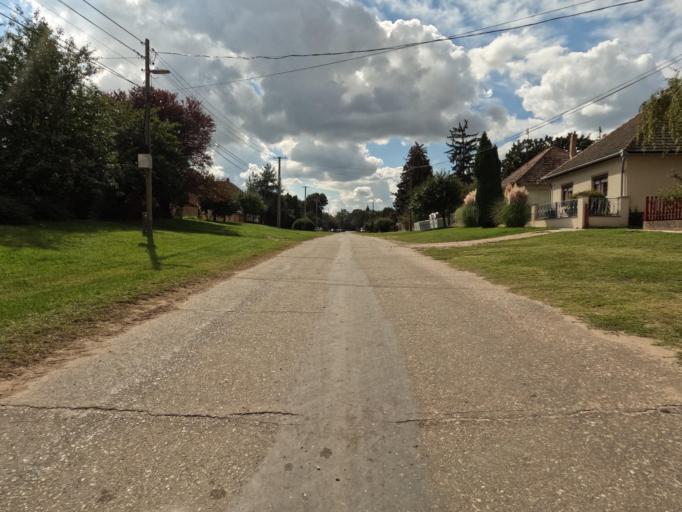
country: HU
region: Tolna
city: Tengelic
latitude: 46.5304
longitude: 18.7154
